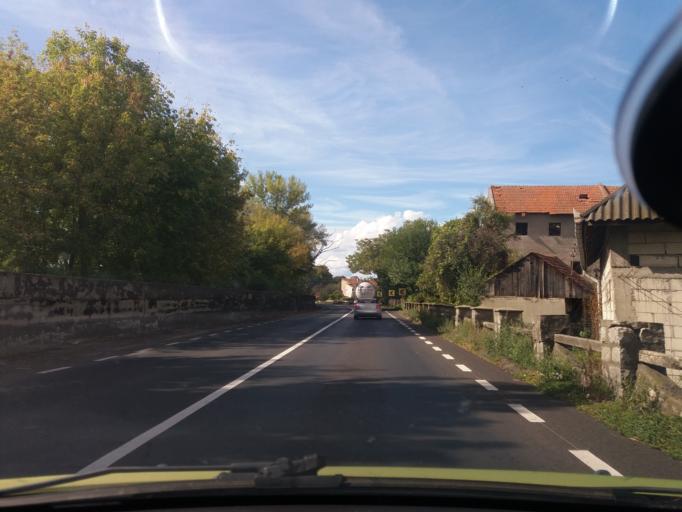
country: RO
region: Hunedoara
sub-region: Comuna Ilia
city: Ilia
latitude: 45.9324
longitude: 22.6552
